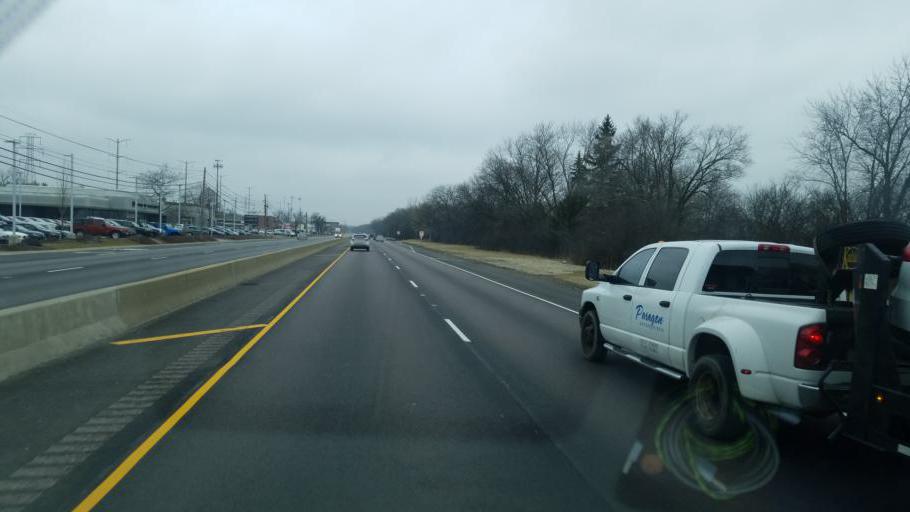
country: US
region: Illinois
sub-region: Lake County
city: Highwood
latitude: 42.2067
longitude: -87.8370
